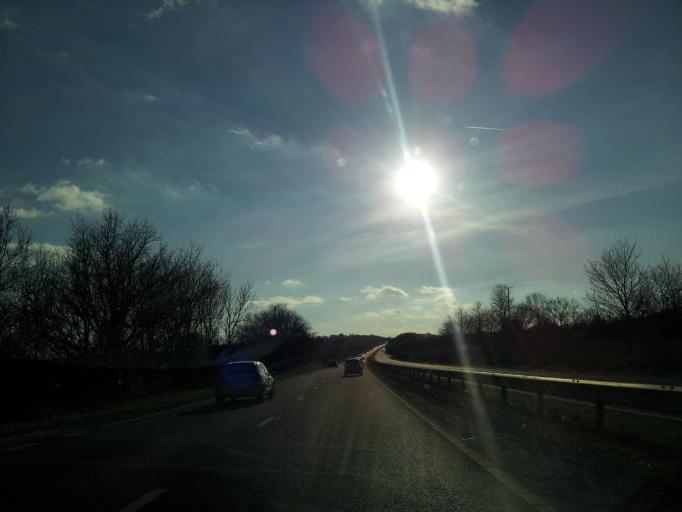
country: GB
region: England
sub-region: Devon
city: Crediton
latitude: 50.7283
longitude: -3.7639
